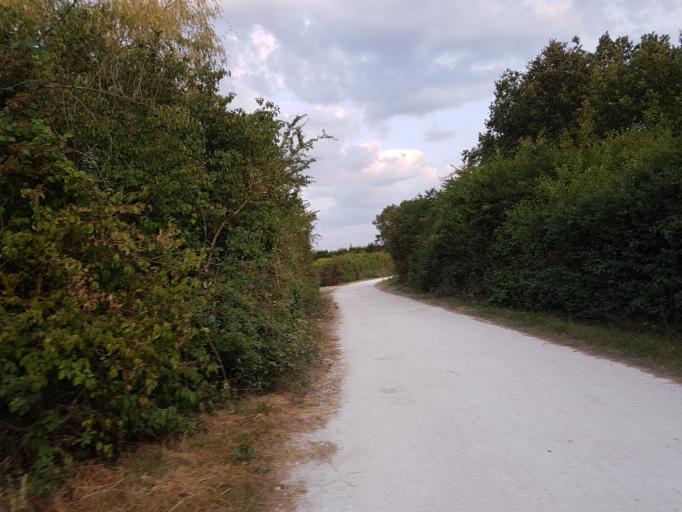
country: FR
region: Centre
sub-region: Departement d'Indre-et-Loire
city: Saint-Avertin
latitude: 47.3547
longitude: 0.7592
